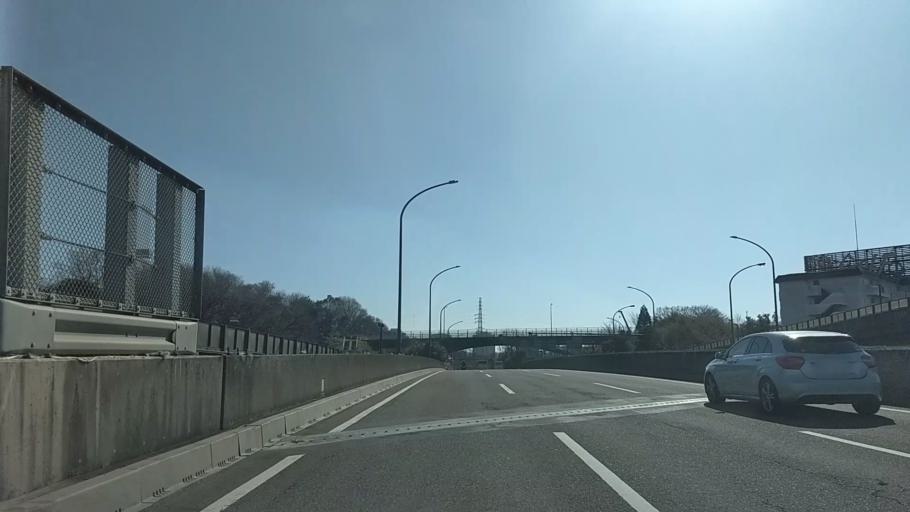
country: JP
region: Kanagawa
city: Yokohama
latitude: 35.4429
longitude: 139.5606
